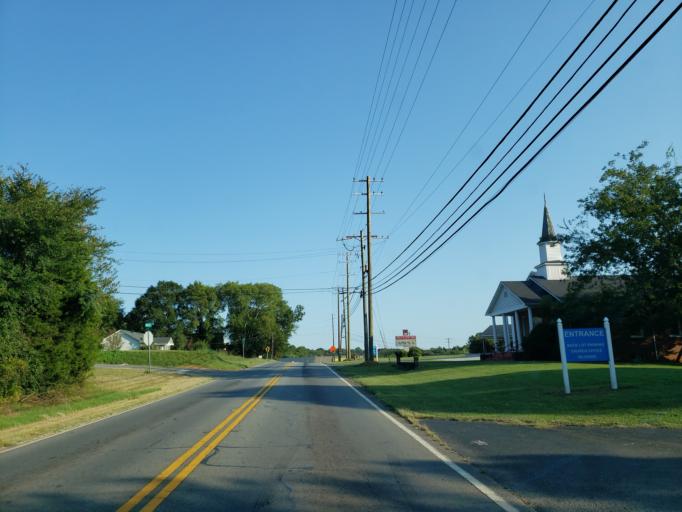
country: US
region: Georgia
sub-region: Murray County
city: Chatsworth
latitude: 34.7568
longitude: -84.8196
